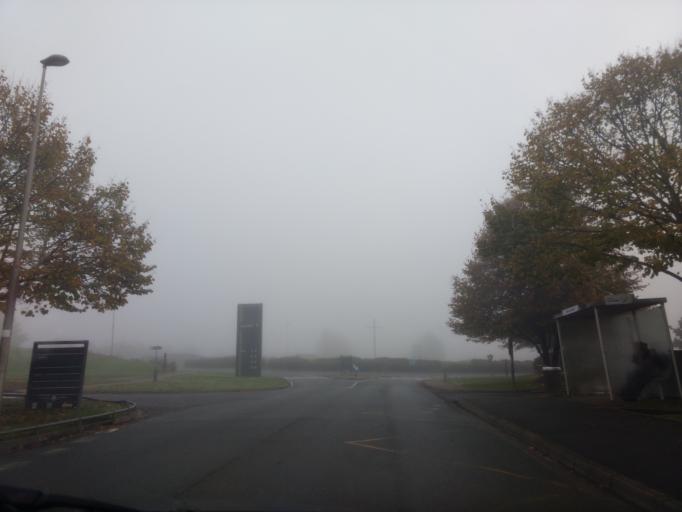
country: FR
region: Poitou-Charentes
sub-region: Departement de la Vienne
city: Chasseneuil-du-Poitou
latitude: 46.6604
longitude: 0.3654
